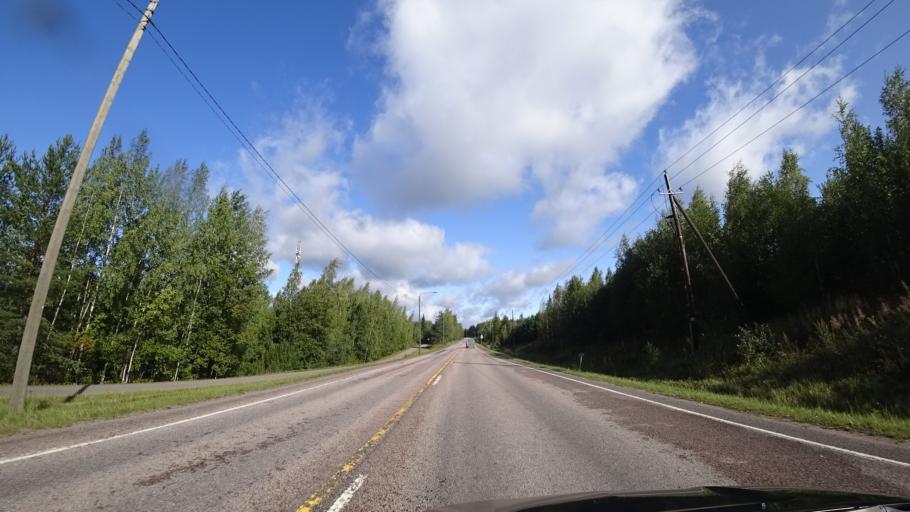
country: FI
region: Uusimaa
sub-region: Helsinki
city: Tuusula
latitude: 60.4183
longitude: 25.0002
